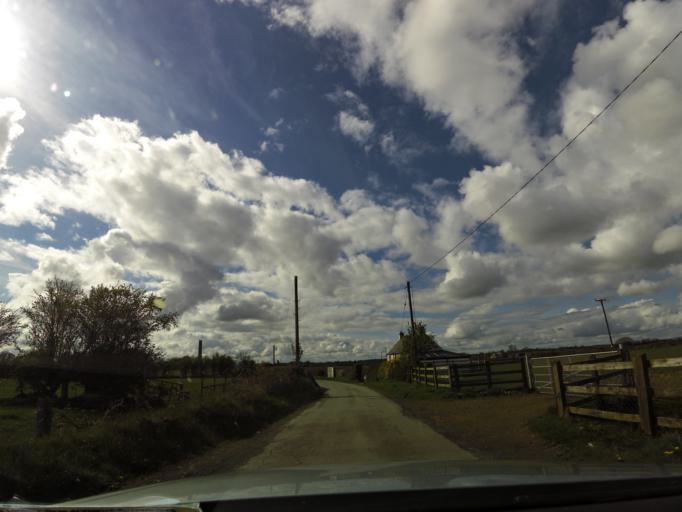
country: IE
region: Leinster
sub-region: Laois
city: Rathdowney
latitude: 52.7775
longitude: -7.5379
